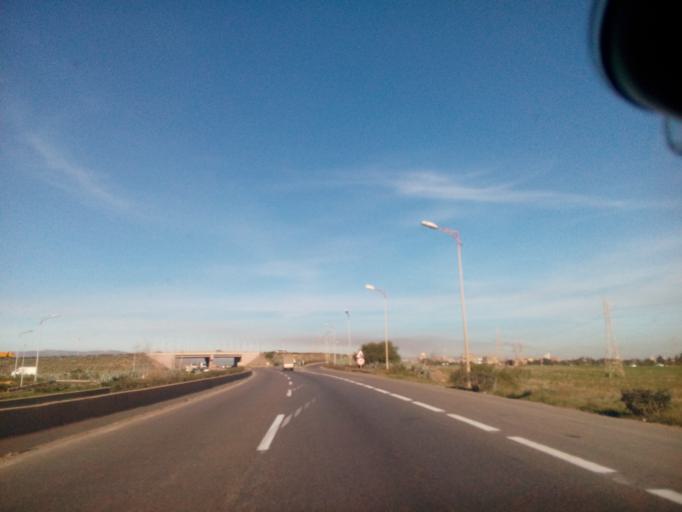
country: DZ
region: Oran
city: Ain el Bya
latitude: 35.7981
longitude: -0.2920
